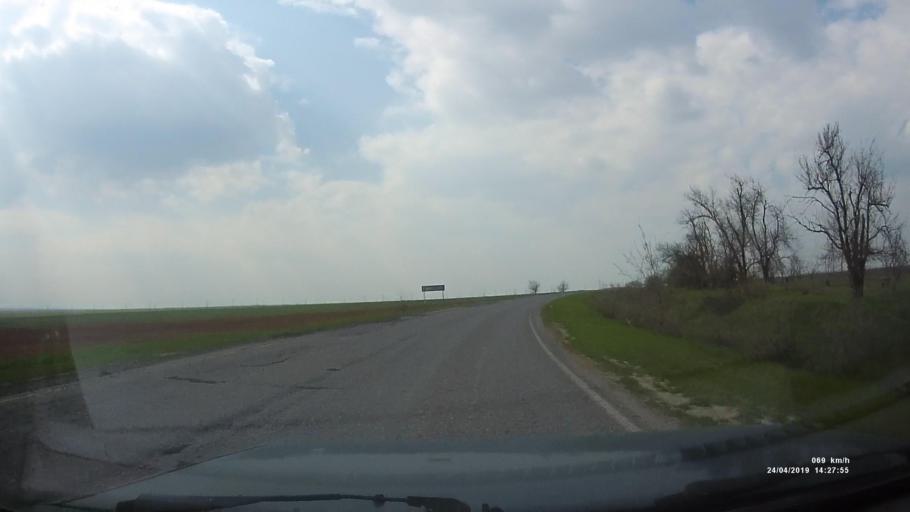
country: RU
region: Kalmykiya
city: Arshan'
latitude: 46.3346
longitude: 44.0348
